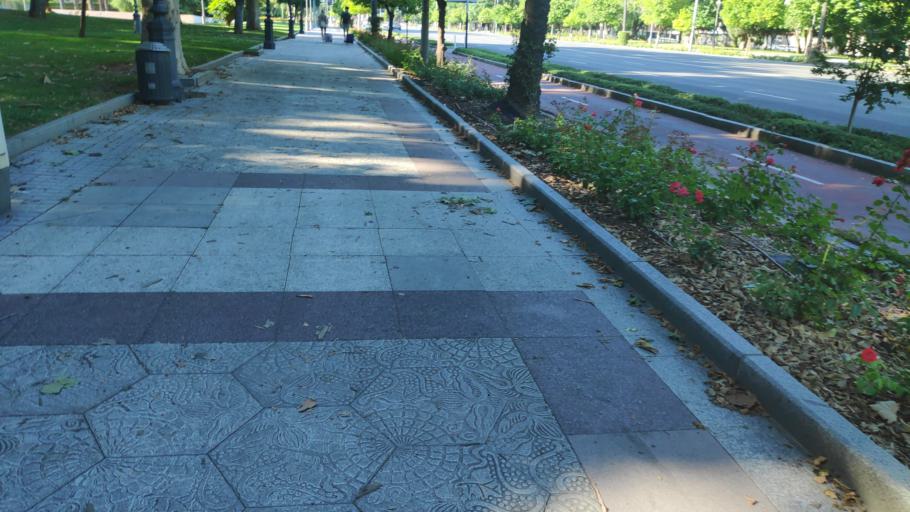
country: ES
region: Andalusia
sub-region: Province of Cordoba
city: Cordoba
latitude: 37.8771
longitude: -4.7863
